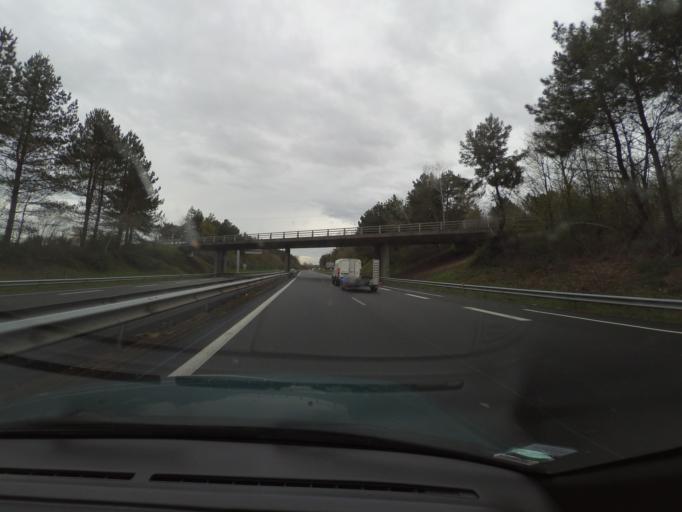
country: FR
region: Pays de la Loire
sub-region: Departement de Maine-et-Loire
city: Seiches-sur-le-Loir
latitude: 47.5685
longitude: -0.3325
